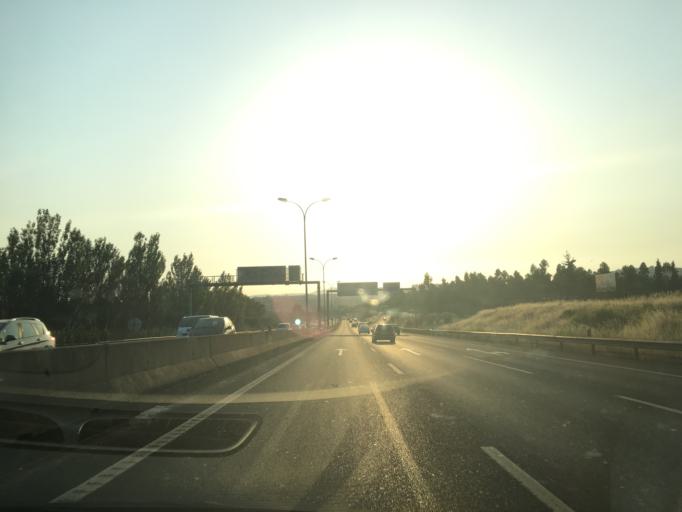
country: PT
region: Lisbon
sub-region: Amadora
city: Amadora
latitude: 38.7475
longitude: -9.2409
